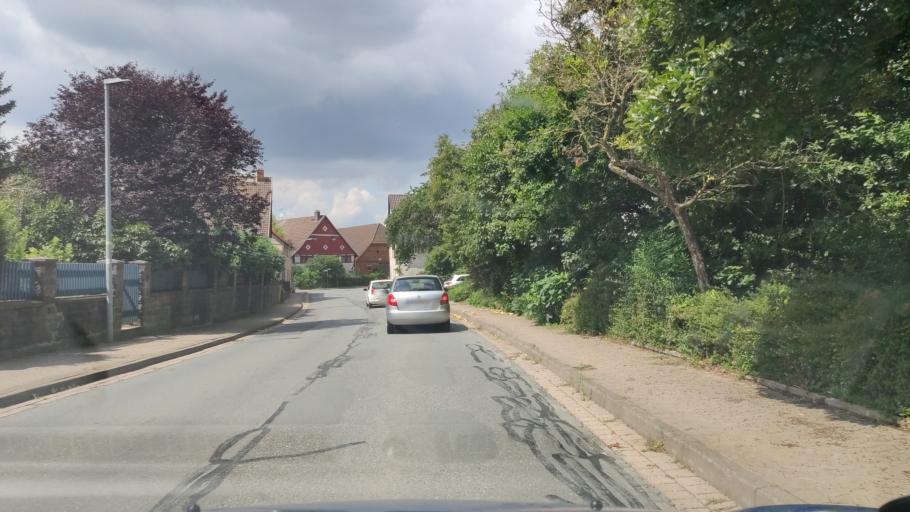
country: DE
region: Lower Saxony
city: Coppenbrugge
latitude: 52.0824
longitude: 9.5034
